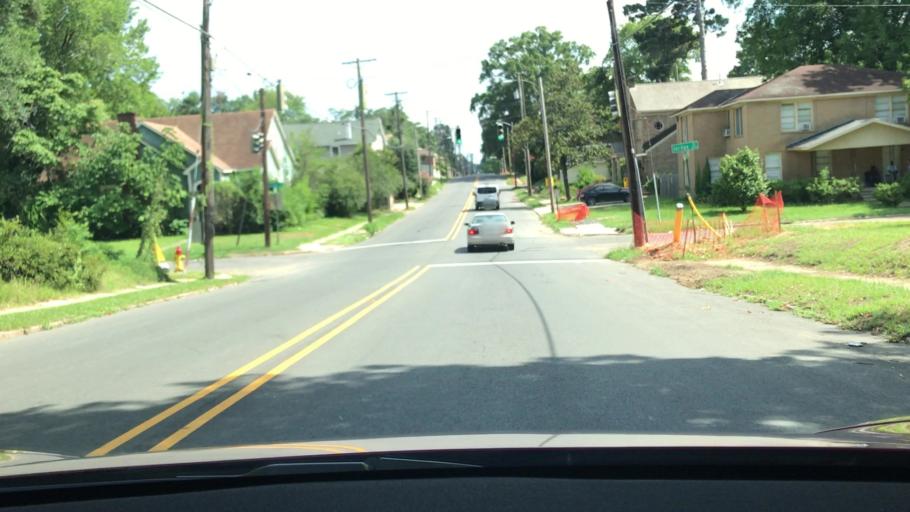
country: US
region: Louisiana
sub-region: Bossier Parish
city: Bossier City
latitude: 32.4984
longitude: -93.7333
